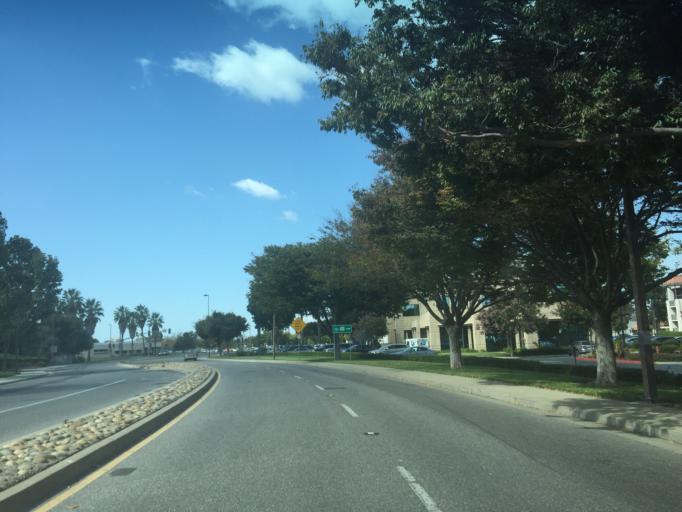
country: US
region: California
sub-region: Santa Clara County
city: Santa Clara
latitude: 37.3904
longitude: -121.9779
